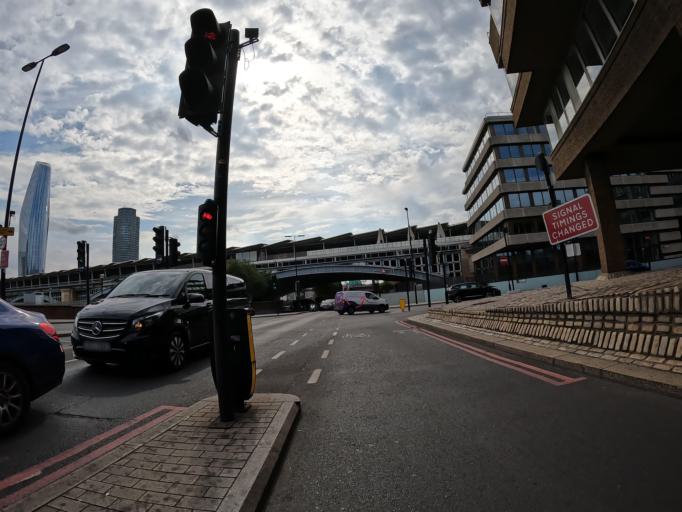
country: GB
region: England
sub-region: Greater London
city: Harringay
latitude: 51.5888
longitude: -0.0942
